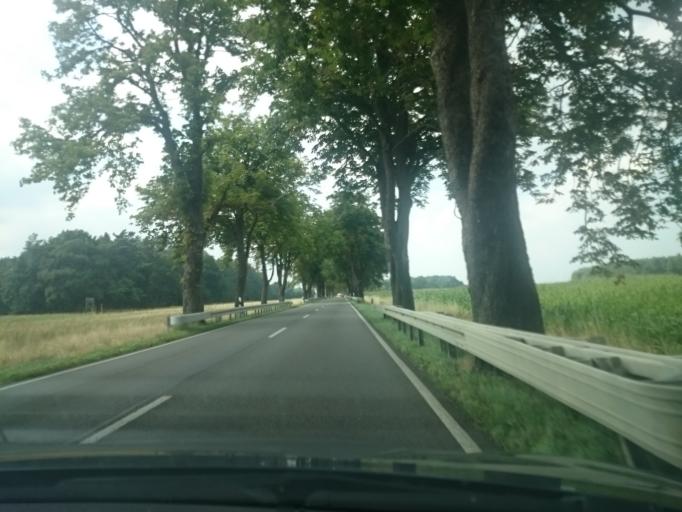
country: DE
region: Mecklenburg-Vorpommern
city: Ducherow
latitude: 53.7295
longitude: 13.8074
